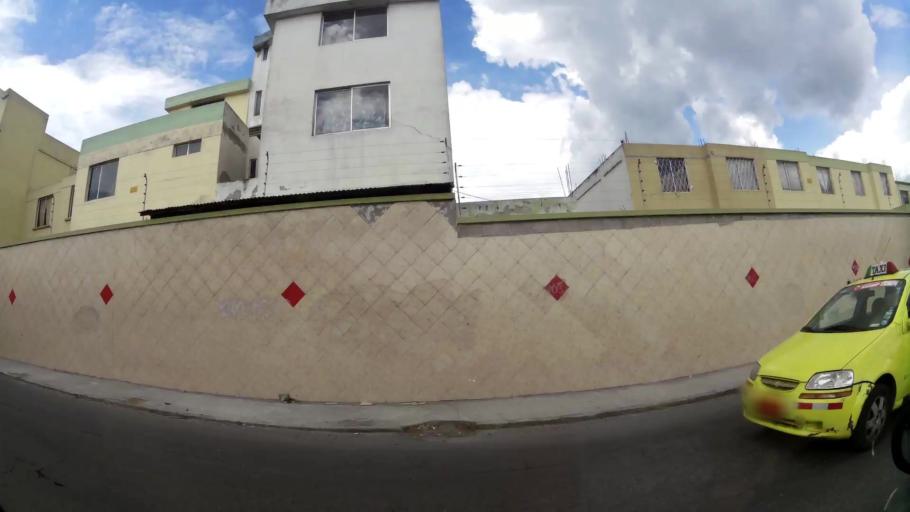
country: EC
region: Pichincha
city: Quito
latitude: -0.0900
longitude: -78.4406
